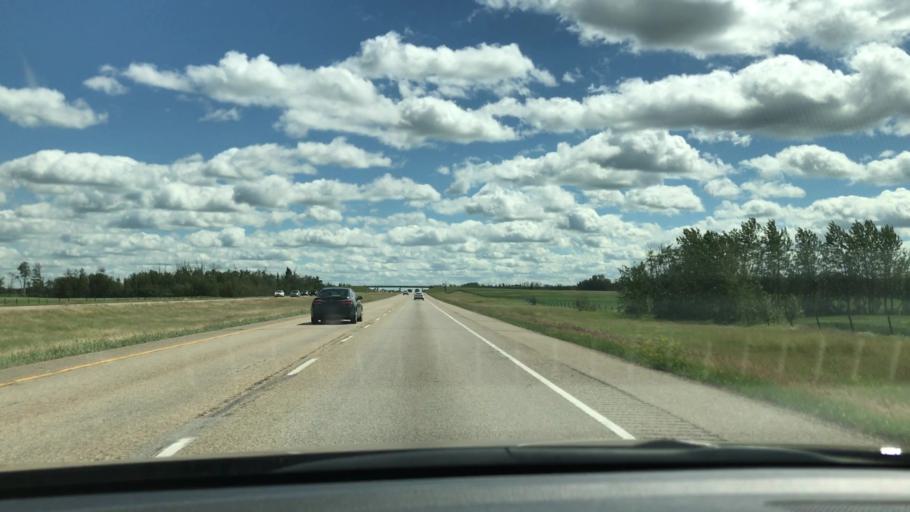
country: CA
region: Alberta
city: Leduc
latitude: 53.1424
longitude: -113.5984
